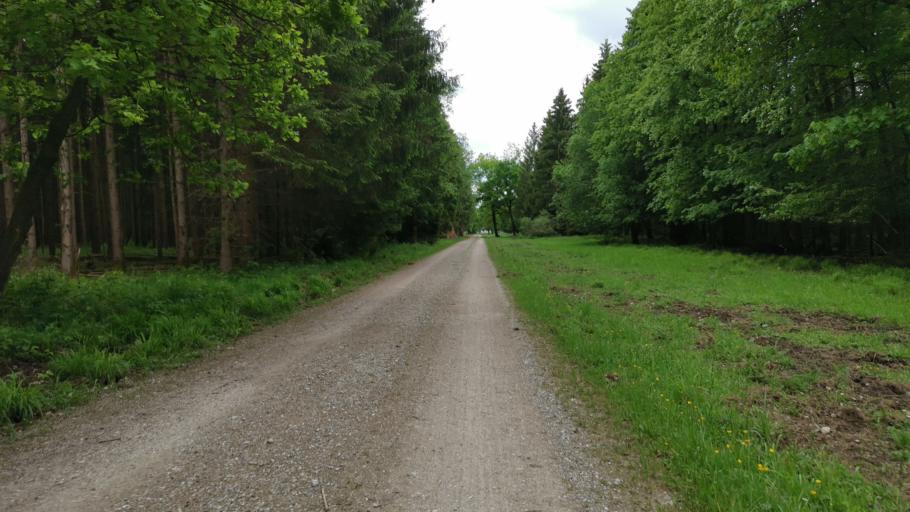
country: DE
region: Bavaria
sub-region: Upper Bavaria
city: Pullach im Isartal
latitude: 48.0600
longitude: 11.4971
